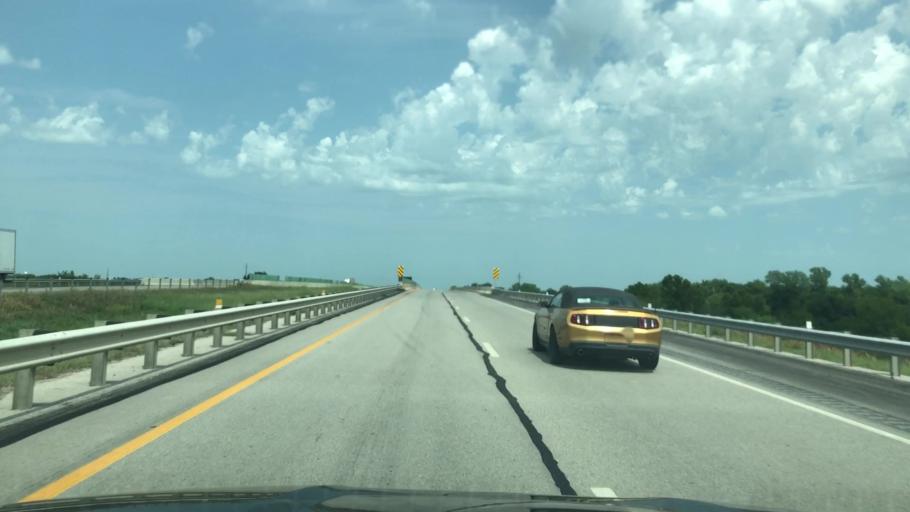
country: US
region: Oklahoma
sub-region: Rogers County
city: Verdigris
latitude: 36.2021
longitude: -95.7094
